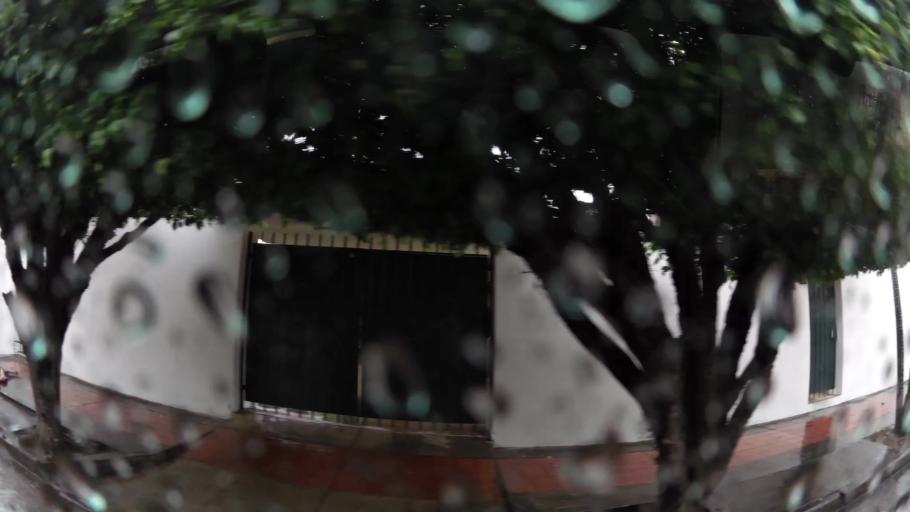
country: BO
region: Santa Cruz
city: Santa Cruz de la Sierra
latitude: -17.8022
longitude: -63.1654
